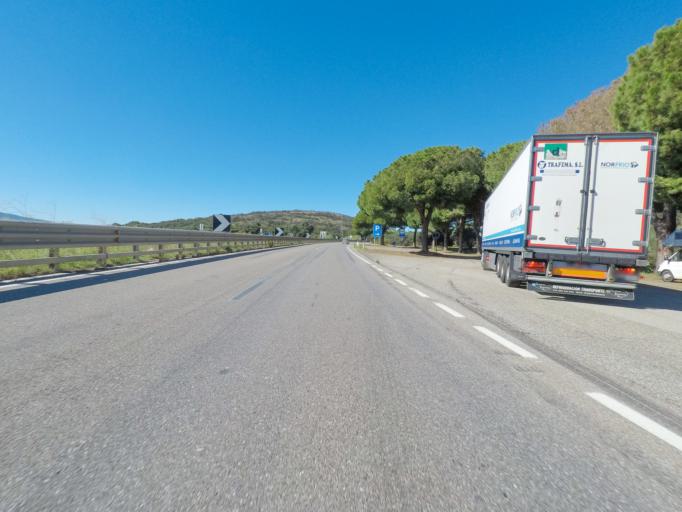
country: IT
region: Tuscany
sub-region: Provincia di Grosseto
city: Orbetello Scalo
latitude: 42.4202
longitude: 11.2914
